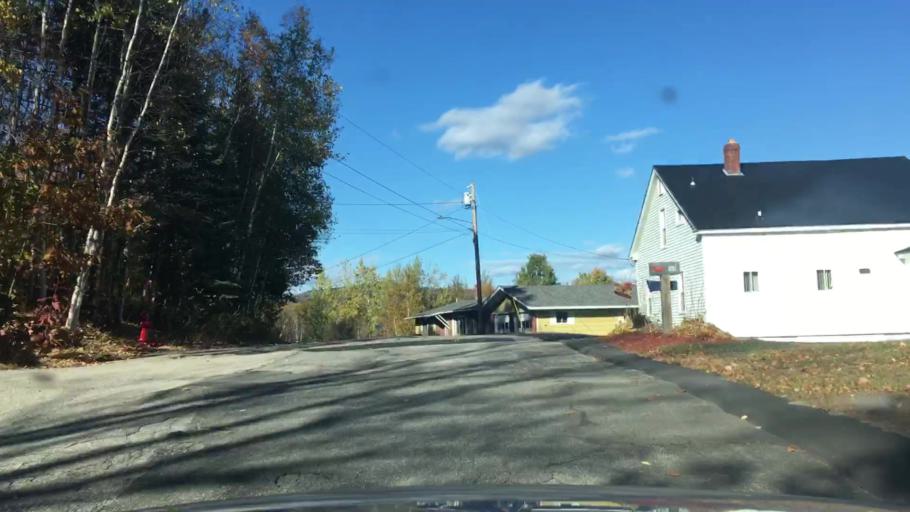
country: US
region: New Hampshire
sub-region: Coos County
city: Berlin
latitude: 44.4687
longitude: -71.1924
